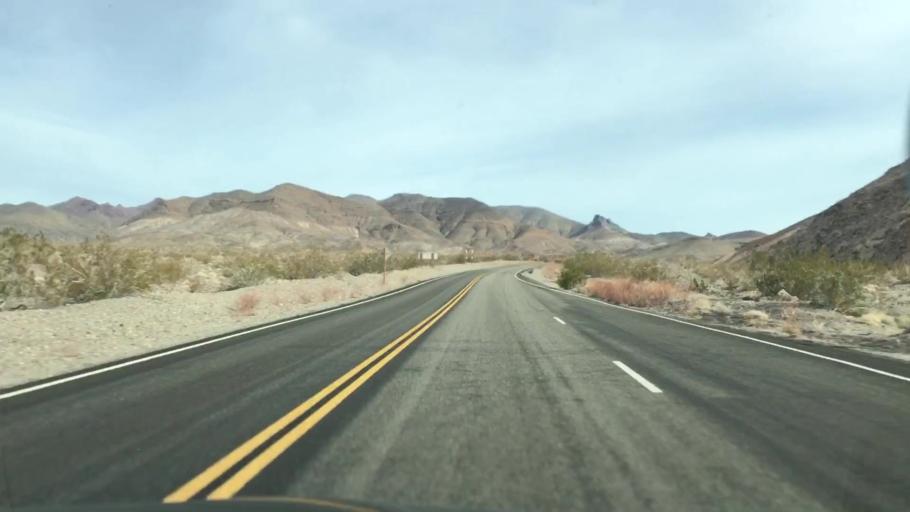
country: US
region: Nevada
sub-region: Nye County
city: Beatty
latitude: 36.7248
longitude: -116.9773
